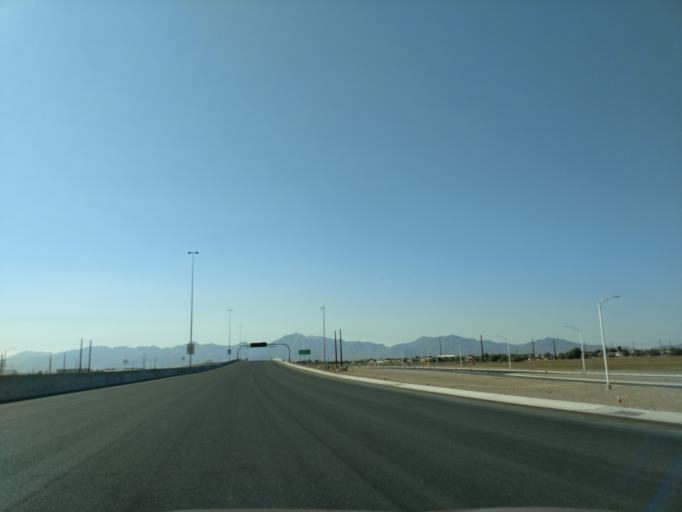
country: US
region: Arizona
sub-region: Maricopa County
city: Laveen
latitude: 33.4259
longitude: -112.1882
